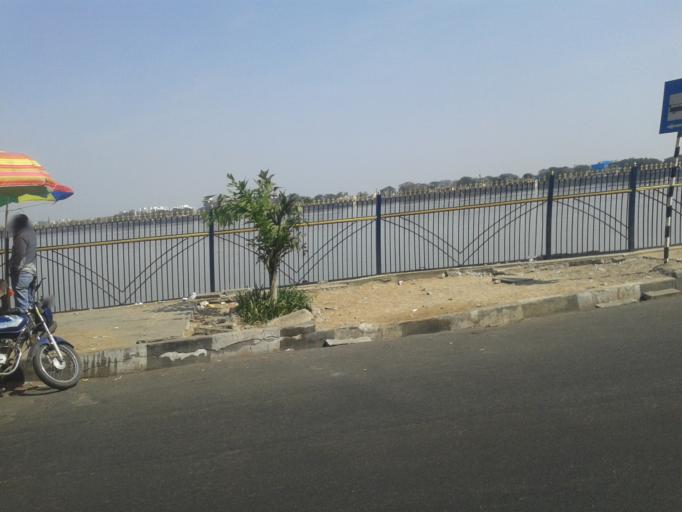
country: IN
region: Telangana
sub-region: Hyderabad
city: Hyderabad
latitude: 17.4131
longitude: 78.4711
